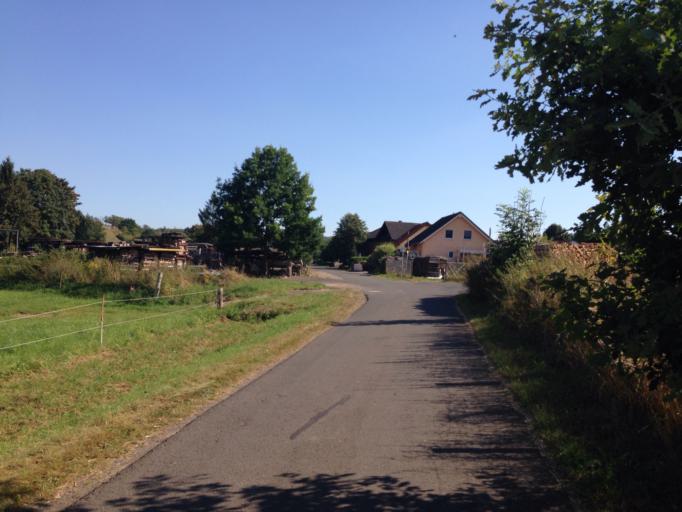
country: DE
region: Hesse
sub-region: Regierungsbezirk Giessen
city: Rabenau
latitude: 50.6502
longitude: 8.8944
